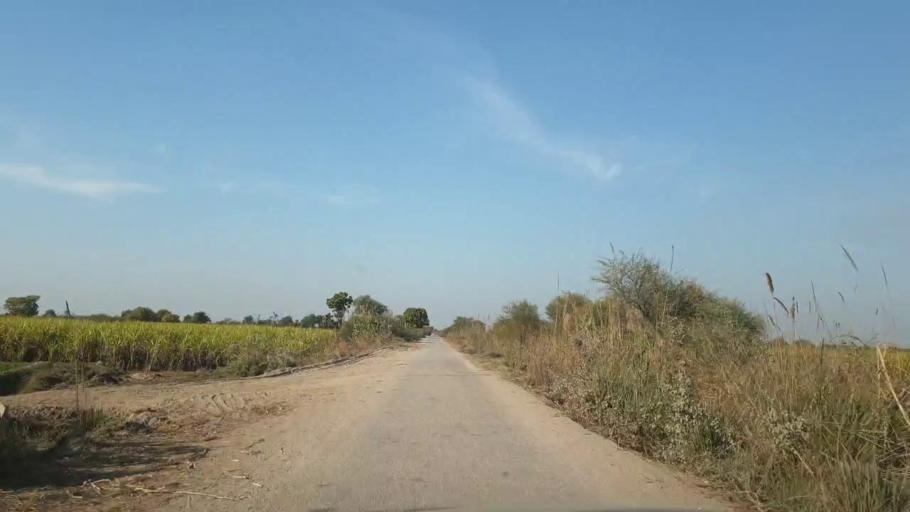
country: PK
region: Sindh
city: Tando Adam
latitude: 25.7219
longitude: 68.7030
